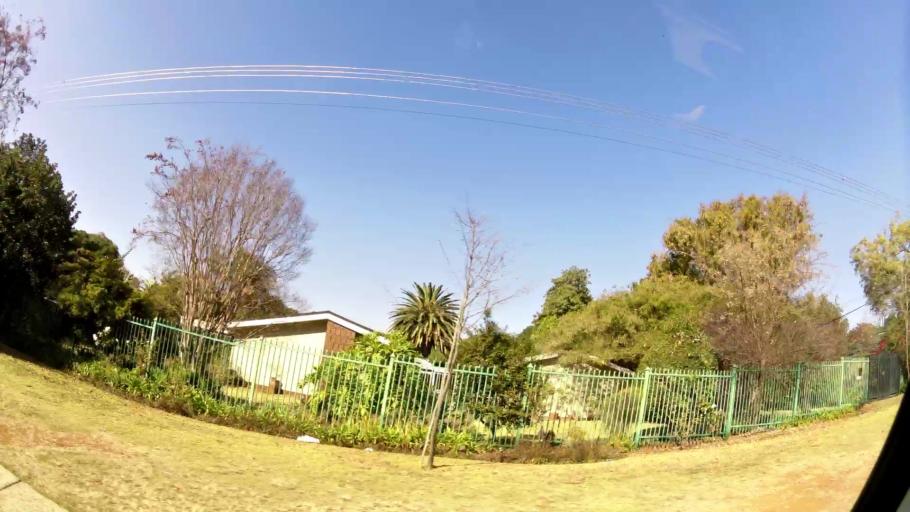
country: ZA
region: Gauteng
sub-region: City of Tshwane Metropolitan Municipality
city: Pretoria
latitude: -25.7853
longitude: 28.2632
